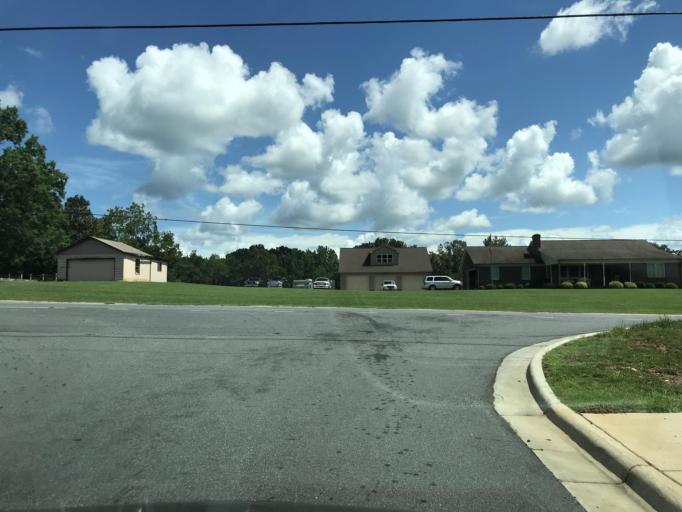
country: US
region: North Carolina
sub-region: Catawba County
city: Lake Norman of Catawba
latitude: 35.5707
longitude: -81.0456
